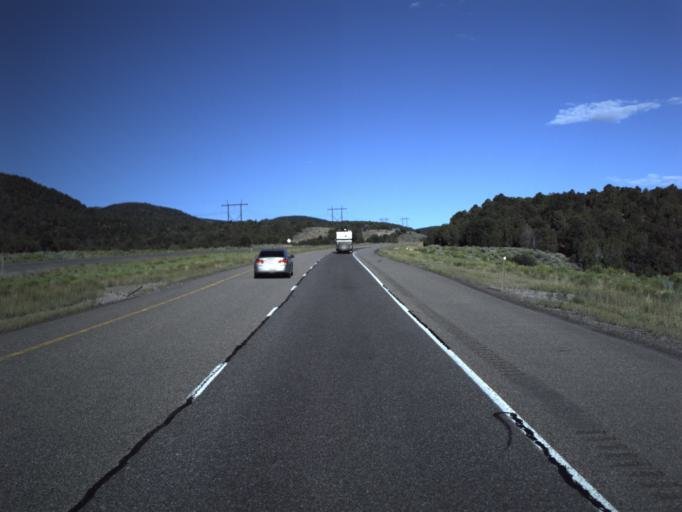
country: US
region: Utah
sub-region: Beaver County
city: Beaver
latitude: 38.5740
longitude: -112.4628
